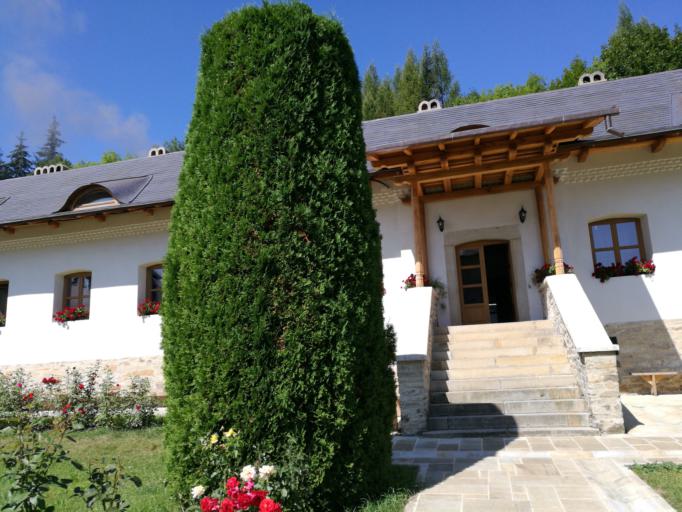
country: RO
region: Suceava
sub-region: Comuna Putna
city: Putna
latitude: 47.8664
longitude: 25.5966
